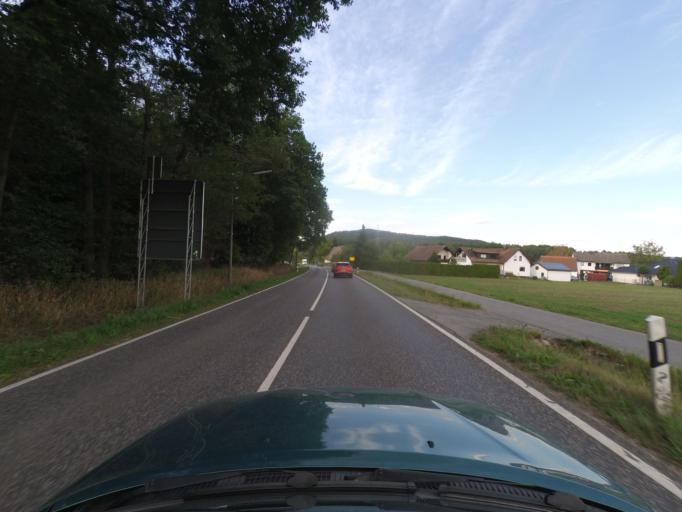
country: DE
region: Bavaria
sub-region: Regierungsbezirk Mittelfranken
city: Altdorf
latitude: 49.3959
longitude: 11.3501
